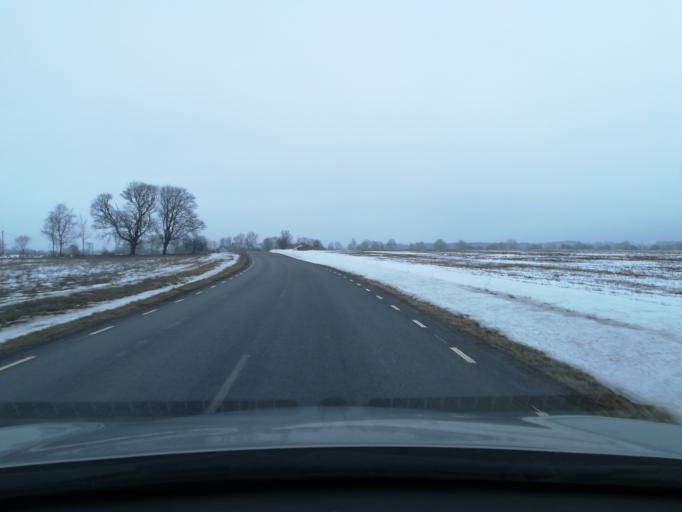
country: EE
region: Harju
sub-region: Kuusalu vald
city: Kuusalu
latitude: 59.4678
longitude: 25.5150
